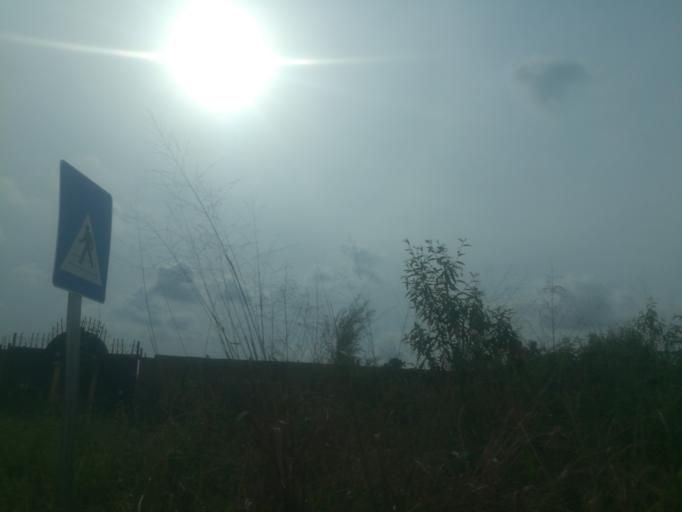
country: NG
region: Ogun
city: Ayetoro
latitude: 7.3355
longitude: 3.0626
